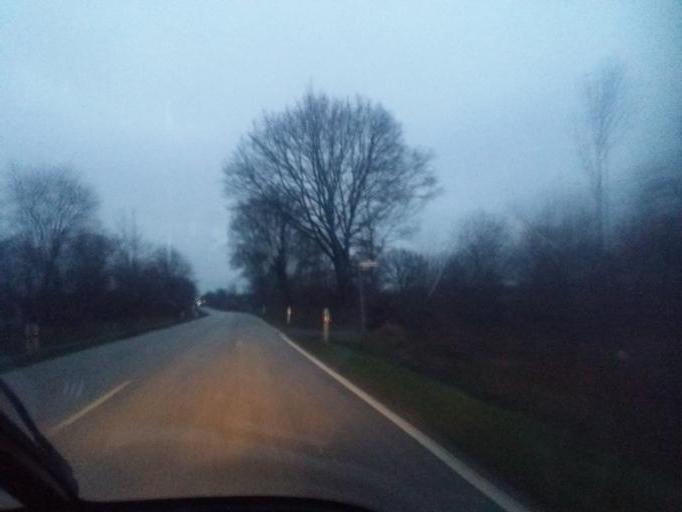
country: DE
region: Schleswig-Holstein
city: Schenefeld
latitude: 54.0589
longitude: 9.4762
